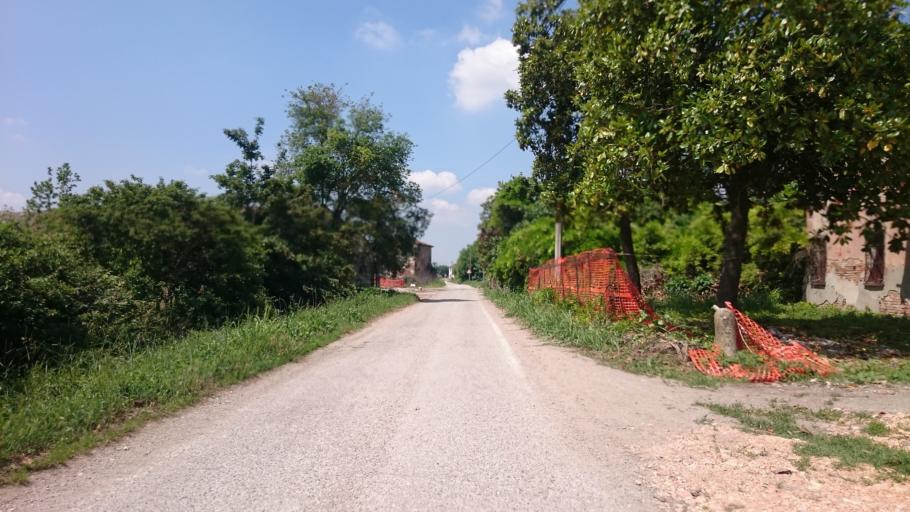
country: IT
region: Lombardy
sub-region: Provincia di Mantova
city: Bagnolo San Vito
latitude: 45.0925
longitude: 10.9194
